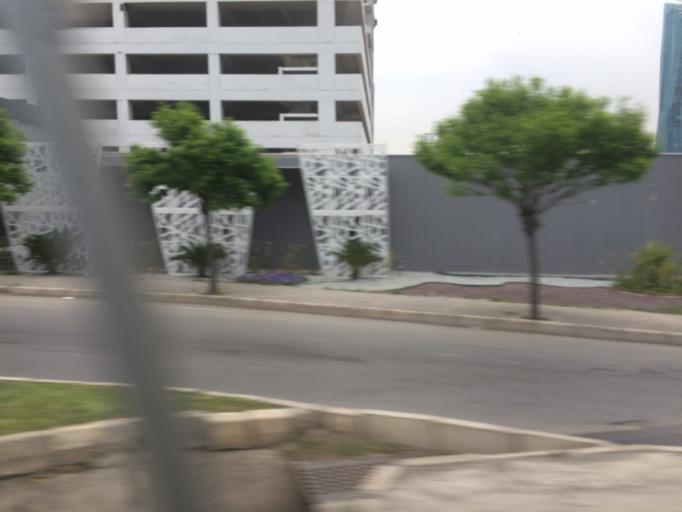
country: TR
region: Izmir
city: Izmir
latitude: 38.4489
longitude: 27.1711
